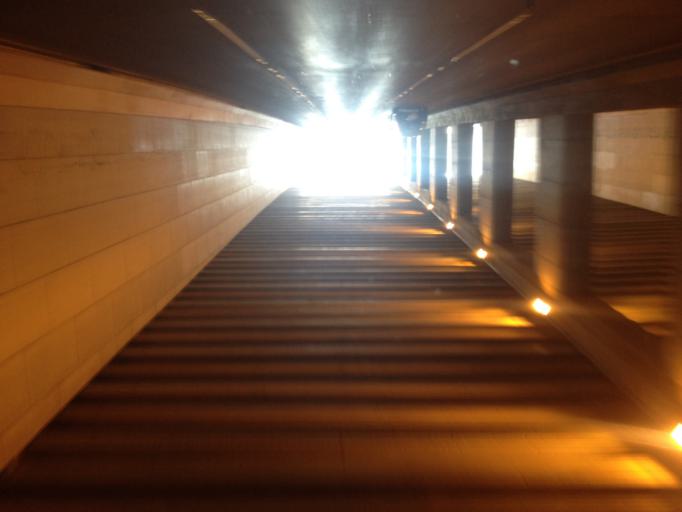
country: BR
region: Federal District
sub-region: Brasilia
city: Brasilia
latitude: -15.8613
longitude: -47.9350
